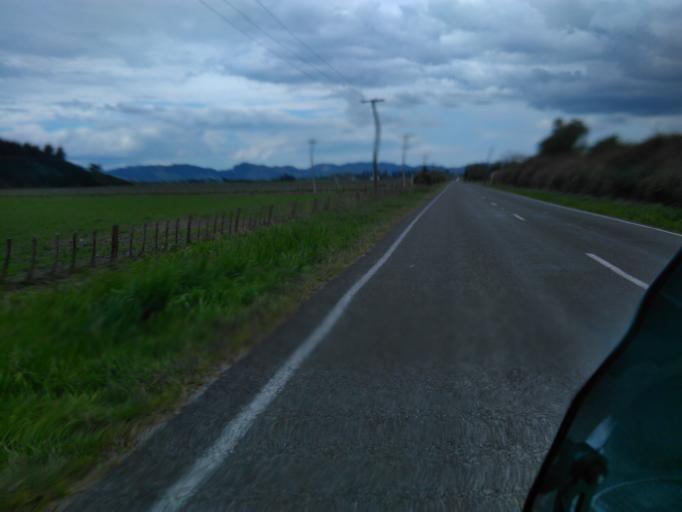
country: NZ
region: Gisborne
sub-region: Gisborne District
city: Gisborne
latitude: -38.6428
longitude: 177.8820
